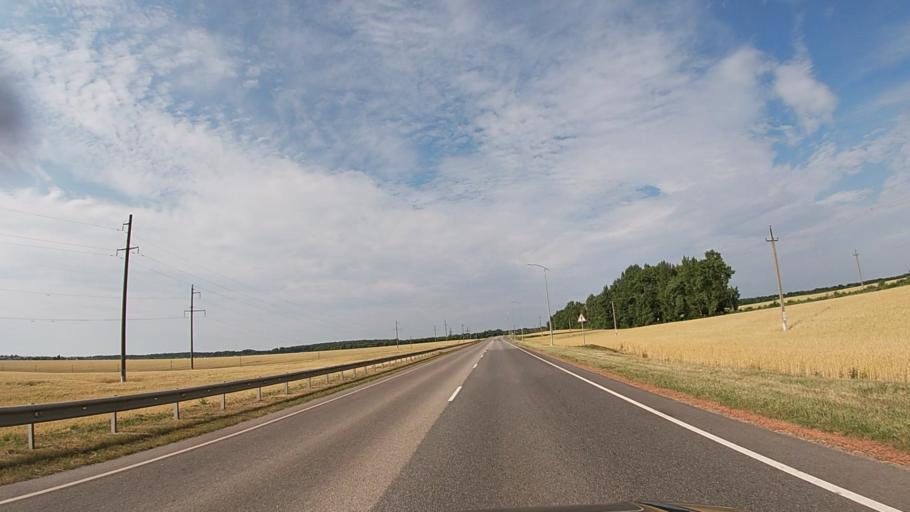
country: RU
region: Belgorod
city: Proletarskiy
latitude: 50.8104
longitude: 35.7470
